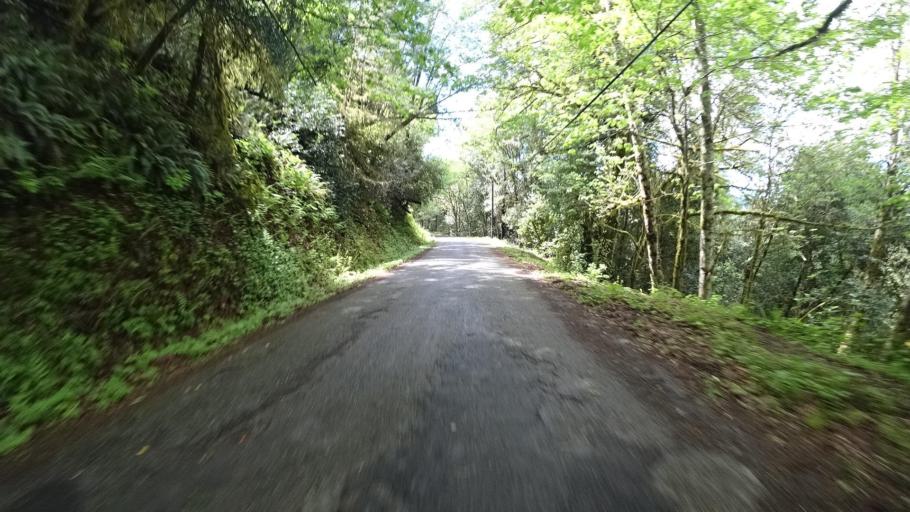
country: US
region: California
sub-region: Humboldt County
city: Blue Lake
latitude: 40.7622
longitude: -123.9005
